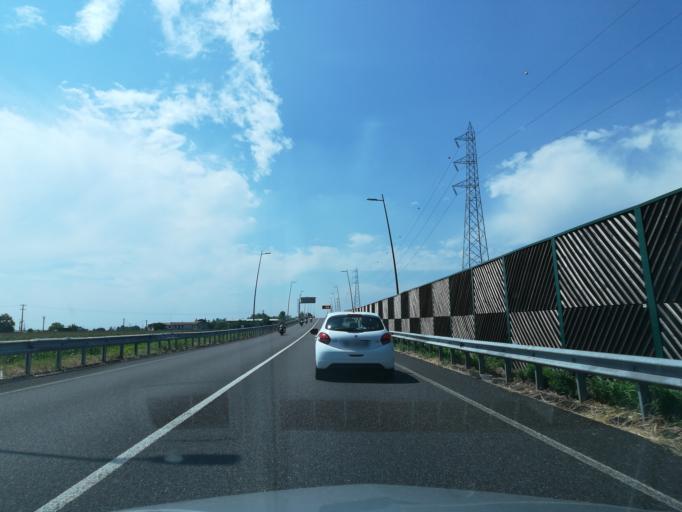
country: IT
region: Lombardy
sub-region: Provincia di Bergamo
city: Comun Nuovo
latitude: 45.6284
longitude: 9.6755
